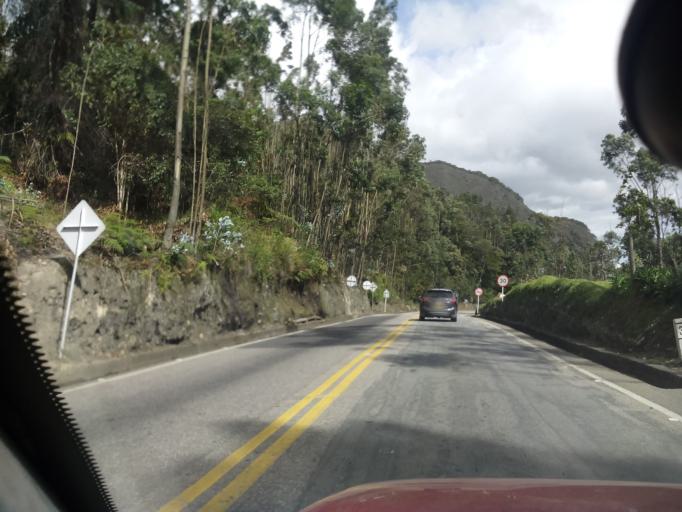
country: CO
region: Boyaca
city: Arcabuco
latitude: 5.7335
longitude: -73.4067
